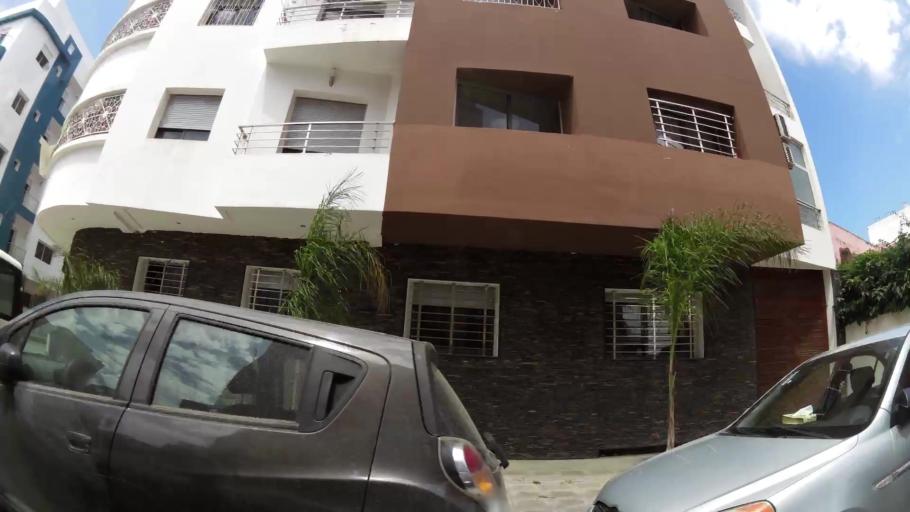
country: MA
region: Gharb-Chrarda-Beni Hssen
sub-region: Kenitra Province
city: Kenitra
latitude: 34.2613
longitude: -6.5954
